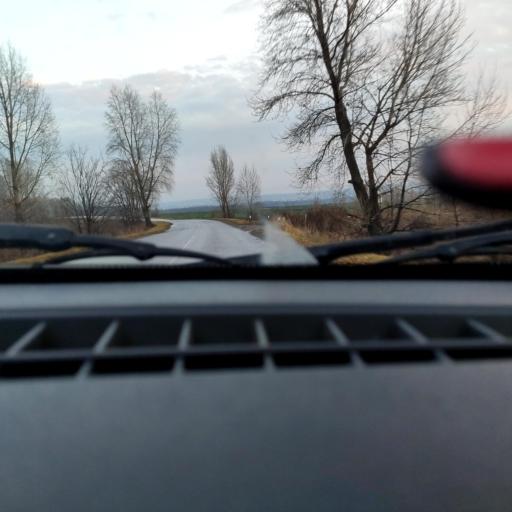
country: RU
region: Bashkortostan
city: Avdon
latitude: 54.5107
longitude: 55.8244
